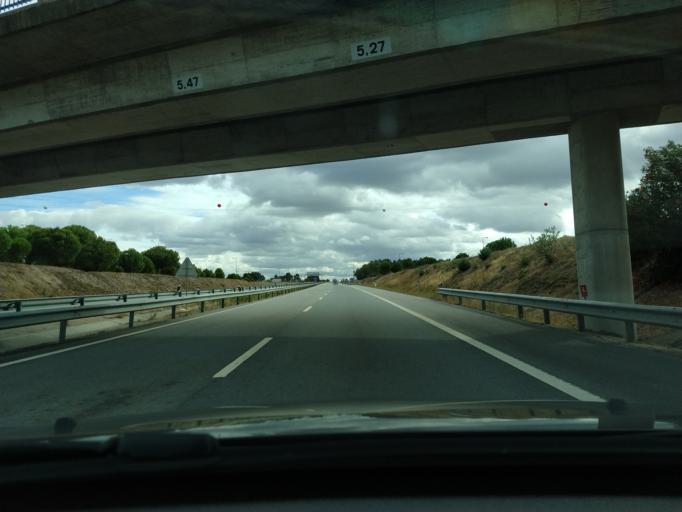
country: PT
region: Guarda
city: Alcains
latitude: 40.0281
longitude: -7.4676
